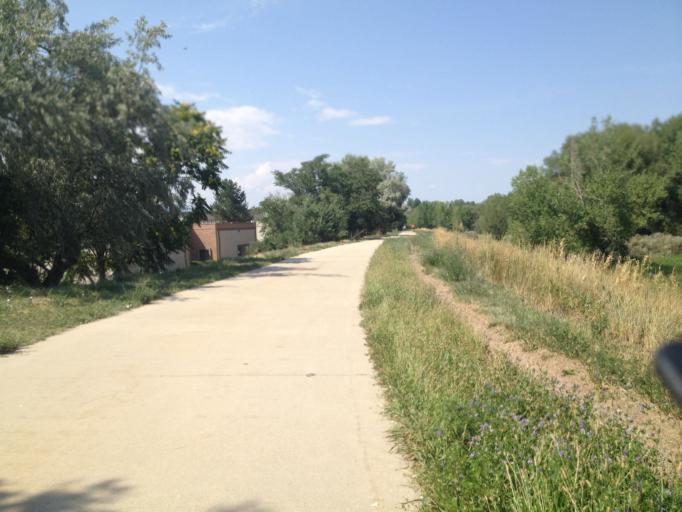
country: US
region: Colorado
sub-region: Boulder County
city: Boulder
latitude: 40.0228
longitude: -105.2165
